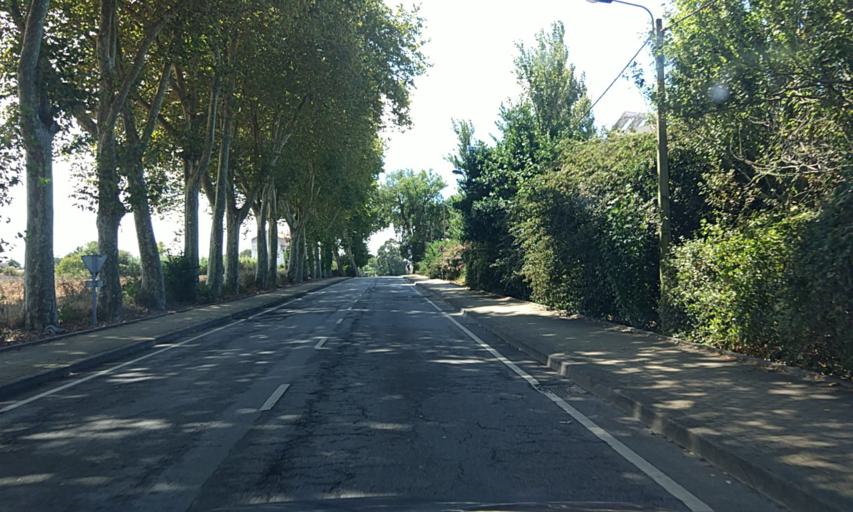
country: PT
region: Aveiro
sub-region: Ilhavo
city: Ilhavo
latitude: 40.5859
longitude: -8.6791
